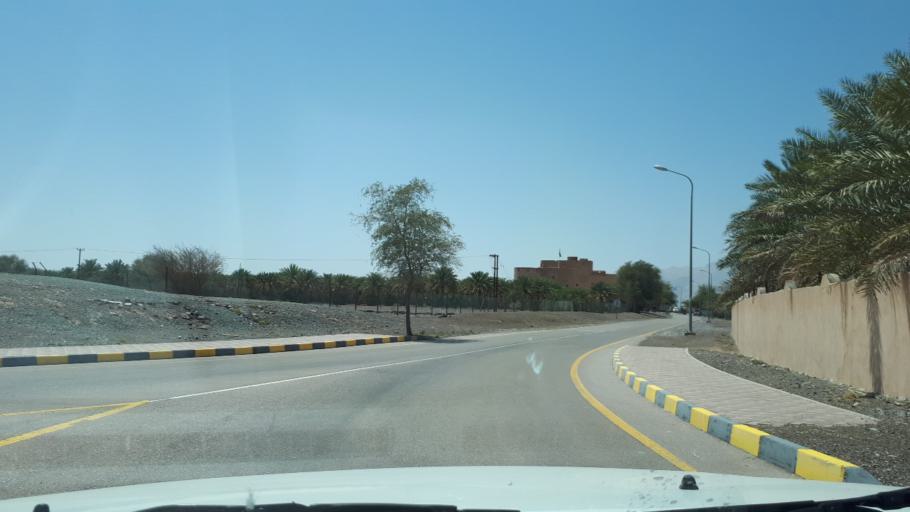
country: OM
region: Muhafazat ad Dakhiliyah
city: Bahla'
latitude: 22.9142
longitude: 57.2519
